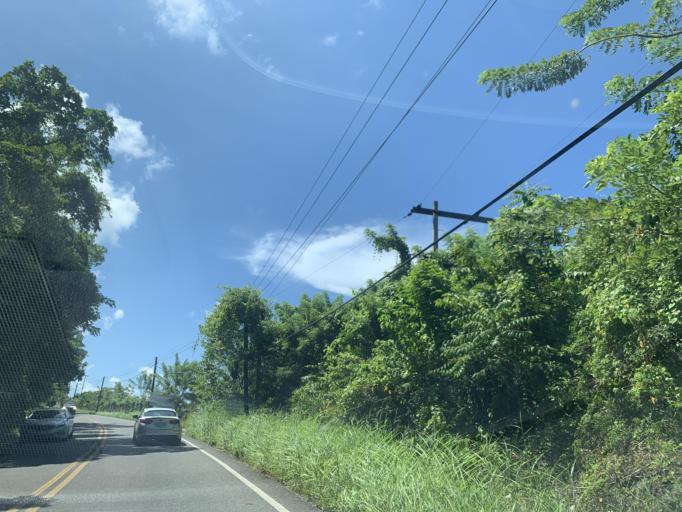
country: DO
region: Maria Trinidad Sanchez
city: Cabrera
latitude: 19.6479
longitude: -69.9231
